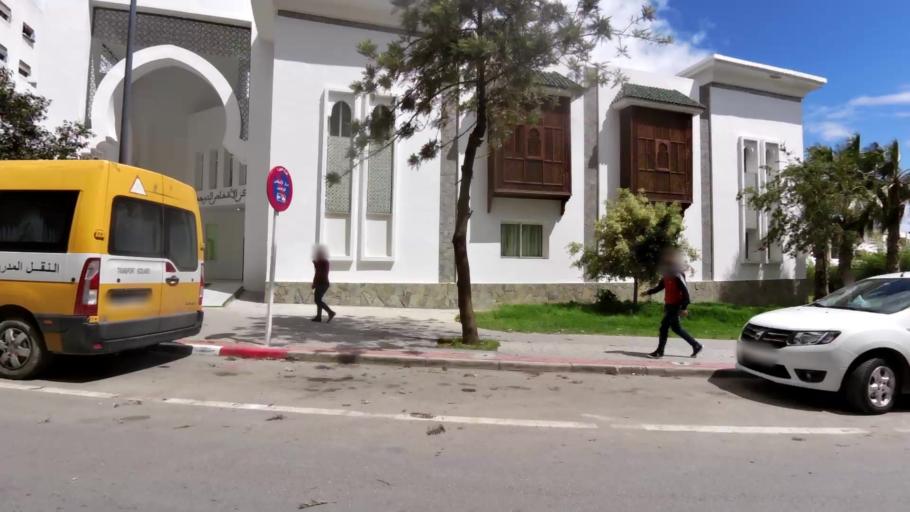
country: MA
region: Tanger-Tetouan
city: Tetouan
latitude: 35.5775
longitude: -5.3506
